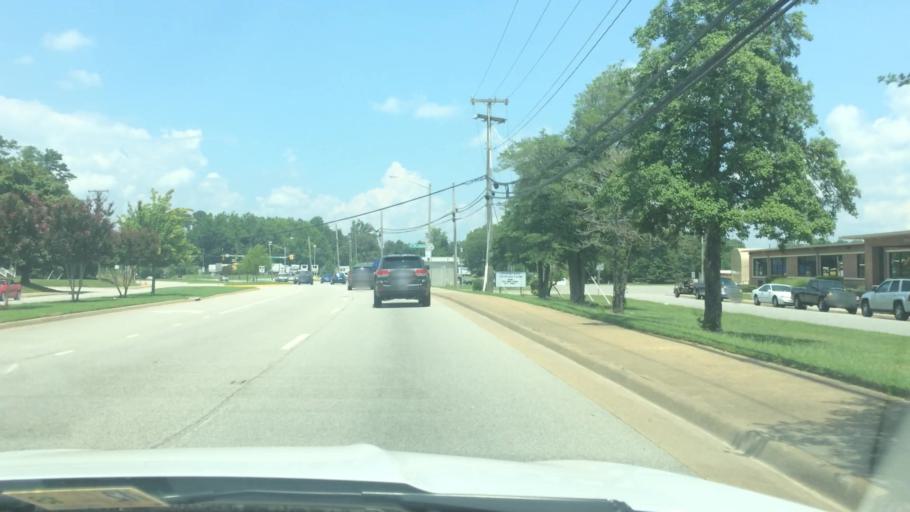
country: US
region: Virginia
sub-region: York County
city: Yorktown
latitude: 37.1624
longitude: -76.5569
